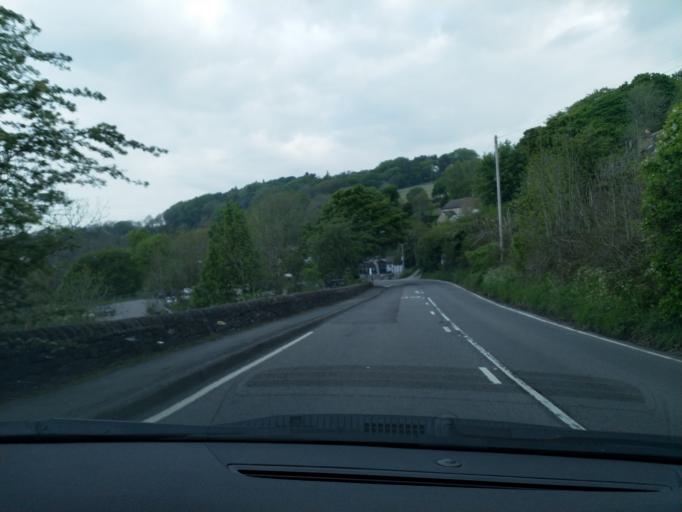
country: GB
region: England
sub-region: Derbyshire
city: Hathersage
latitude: 53.3225
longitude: -1.6395
